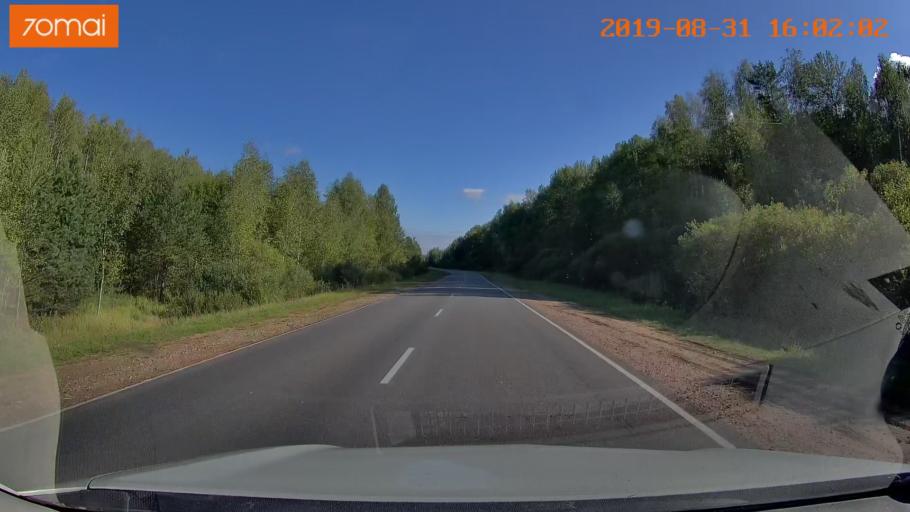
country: RU
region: Kaluga
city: Yukhnov
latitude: 54.6806
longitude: 35.2966
